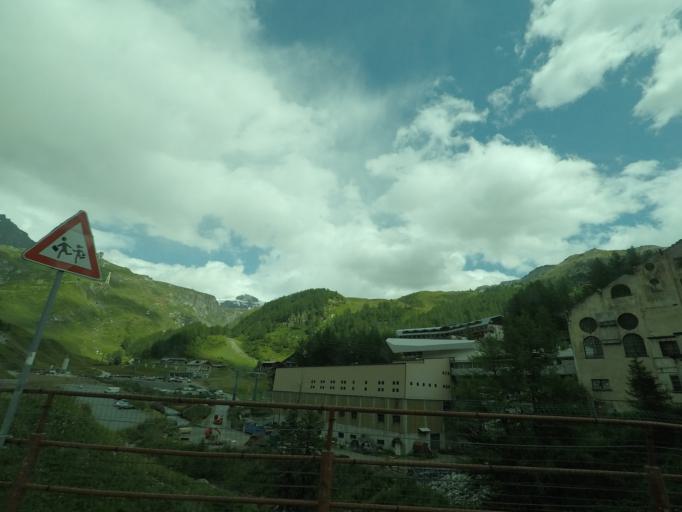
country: IT
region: Aosta Valley
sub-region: Valle d'Aosta
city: Paquier
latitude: 45.9345
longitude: 7.6324
